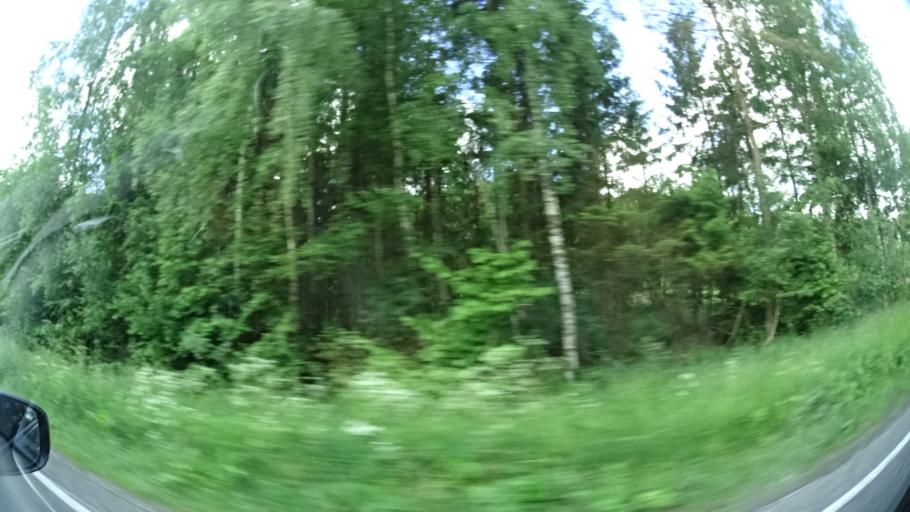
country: DK
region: Central Jutland
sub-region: Syddjurs Kommune
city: Ebeltoft
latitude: 56.2603
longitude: 10.6224
